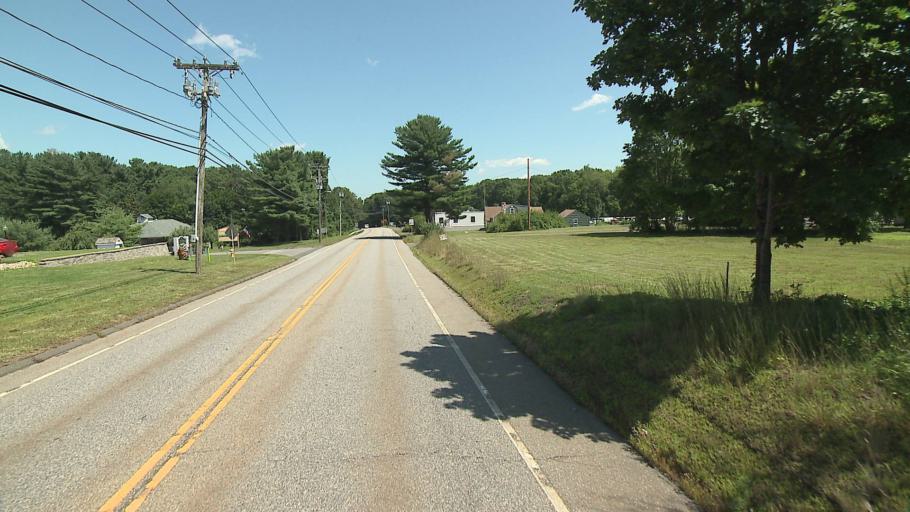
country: US
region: Connecticut
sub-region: Hartford County
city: Collinsville
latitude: 41.7699
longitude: -72.9613
